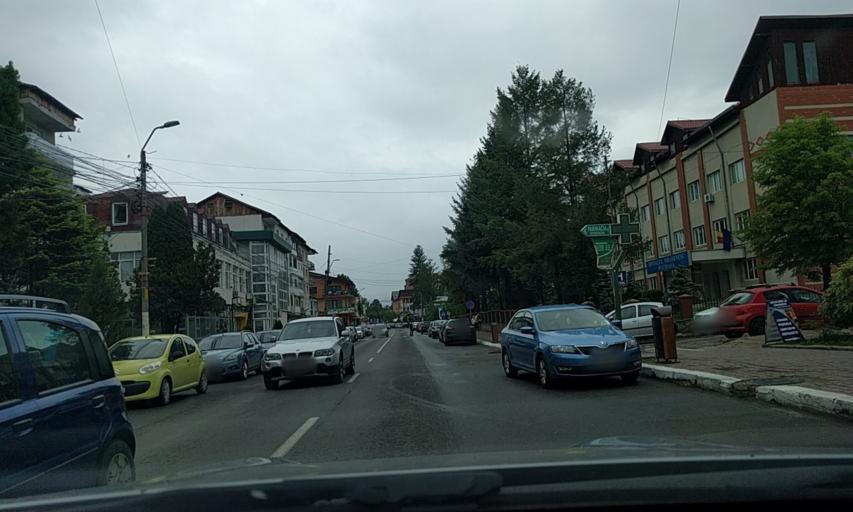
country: RO
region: Dambovita
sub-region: Oras Pucioasa
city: Pucioasa
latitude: 45.0746
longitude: 25.4350
